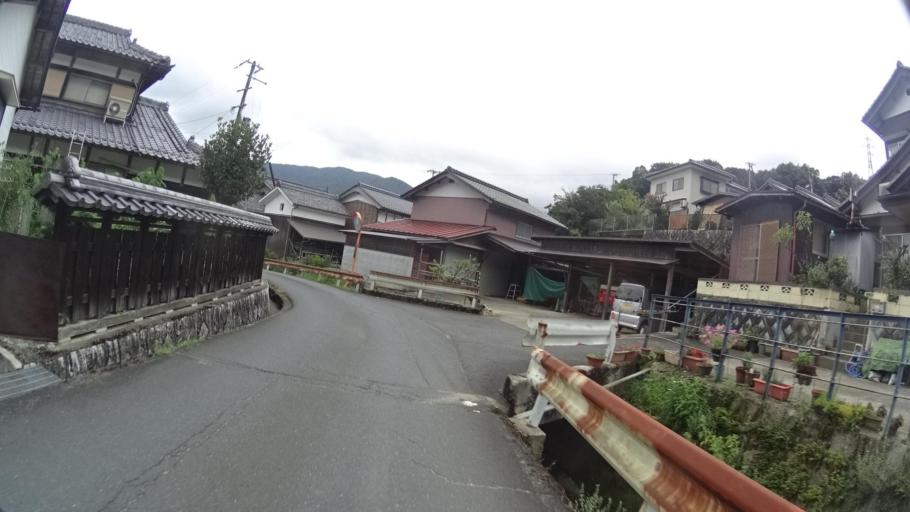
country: JP
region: Kyoto
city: Miyazu
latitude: 35.5277
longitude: 135.1853
